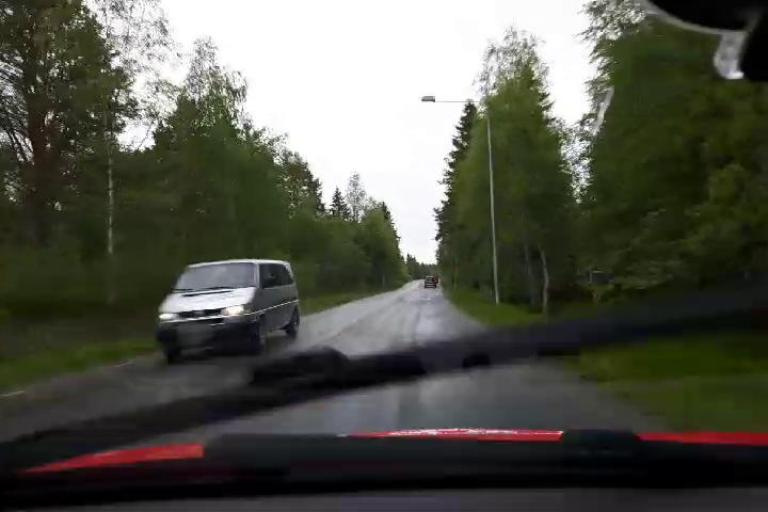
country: SE
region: Jaemtland
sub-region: Bergs Kommun
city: Hoverberg
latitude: 62.7759
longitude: 14.4301
